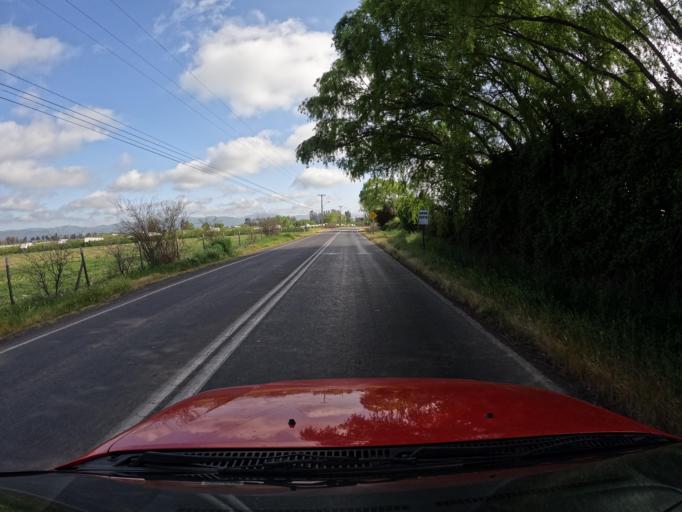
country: CL
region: Maule
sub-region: Provincia de Curico
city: Rauco
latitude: -34.8914
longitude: -71.2741
